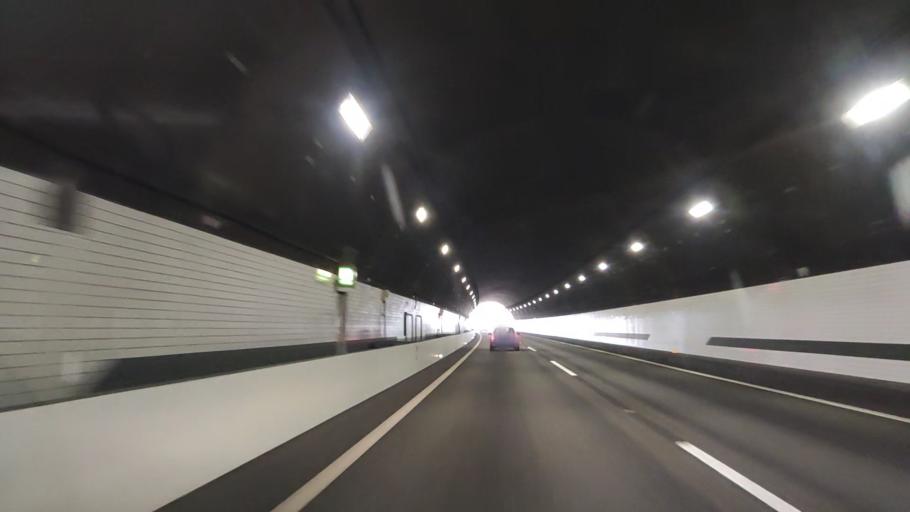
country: JP
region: Tokushima
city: Ishii
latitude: 34.1966
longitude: 134.4320
